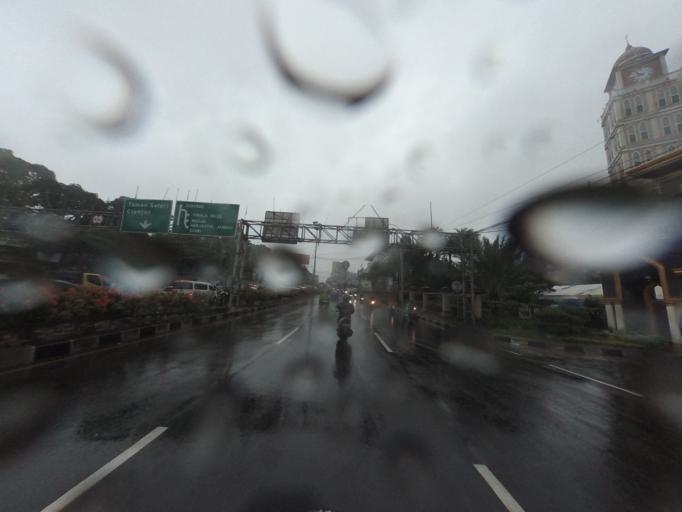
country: ID
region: West Java
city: Caringin
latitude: -6.6555
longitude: 106.8595
